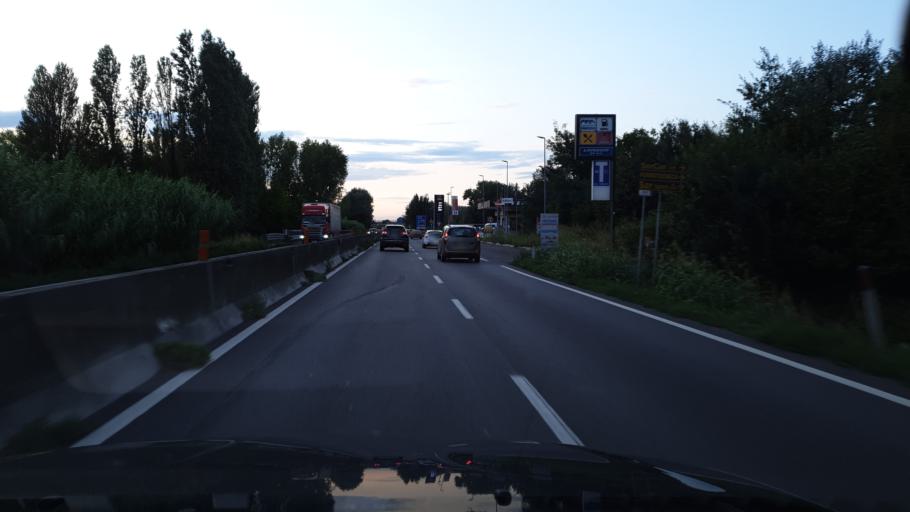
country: IT
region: Emilia-Romagna
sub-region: Provincia di Ravenna
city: Ravenna
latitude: 44.4060
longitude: 12.1760
